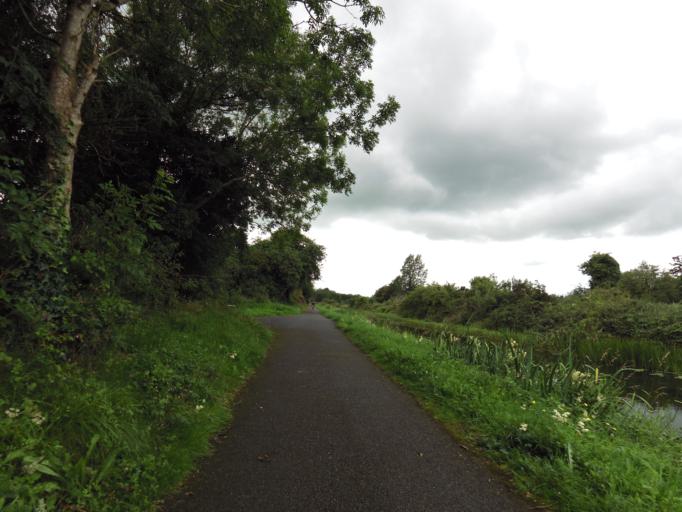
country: IE
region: Leinster
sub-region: An Iarmhi
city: An Muileann gCearr
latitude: 53.5103
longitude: -7.3951
